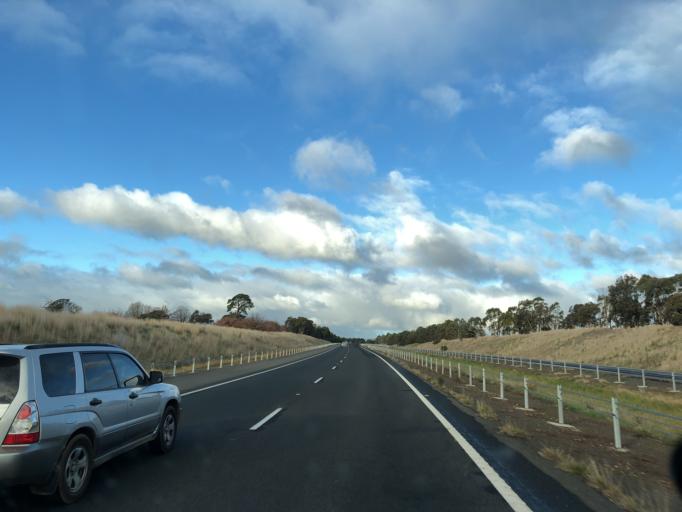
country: AU
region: Victoria
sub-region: Mount Alexander
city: Castlemaine
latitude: -37.2248
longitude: 144.4255
